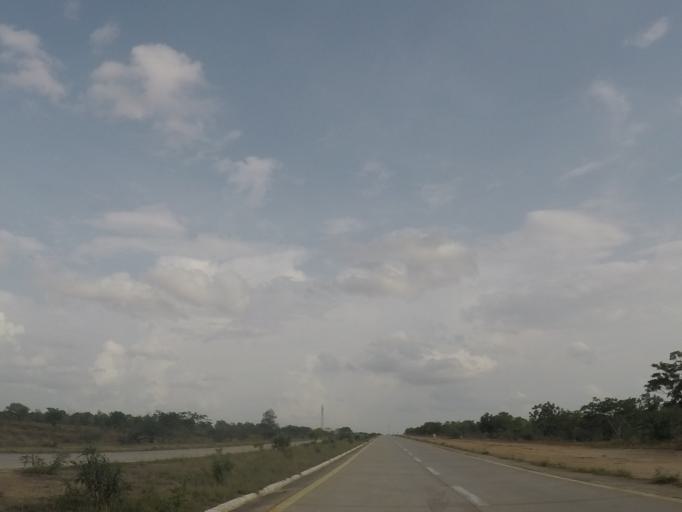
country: MM
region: Mandalay
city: Meiktila
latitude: 20.6470
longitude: 95.8078
